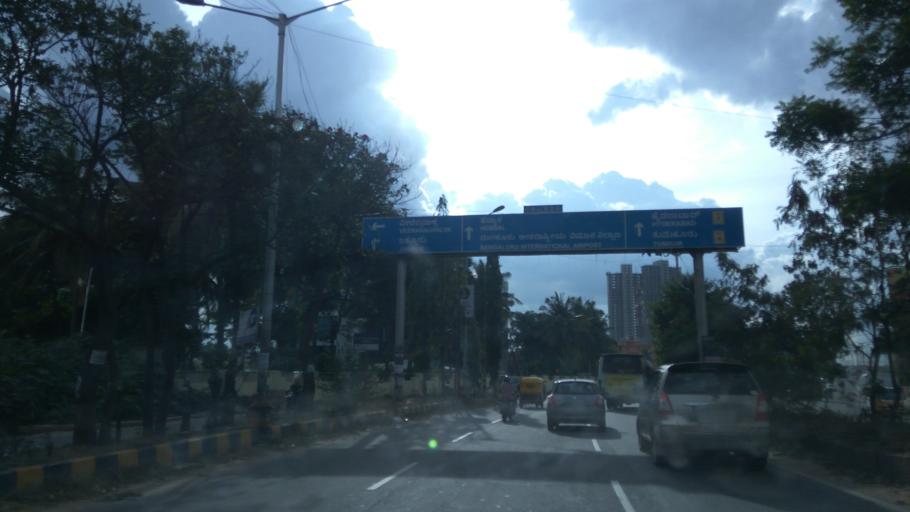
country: IN
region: Karnataka
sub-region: Bangalore Urban
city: Yelahanka
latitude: 13.0409
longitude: 77.6177
